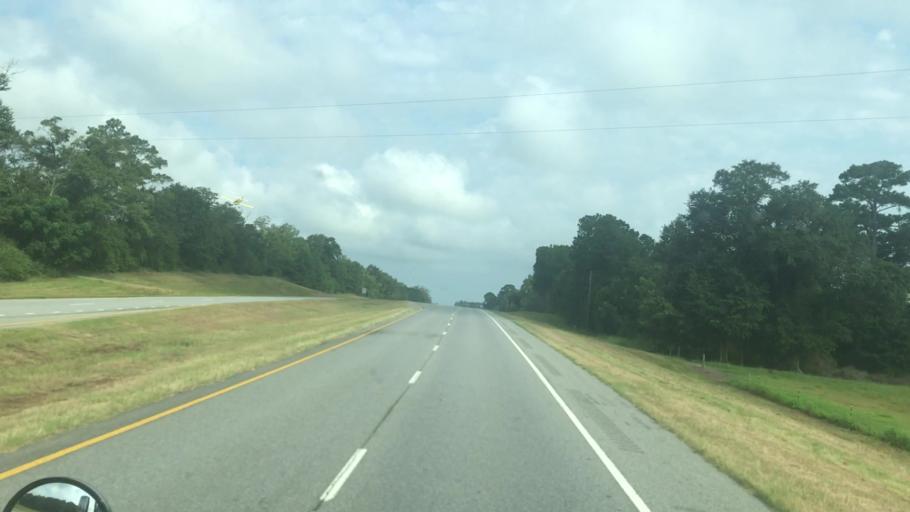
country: US
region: Georgia
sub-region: Miller County
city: Colquitt
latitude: 31.2480
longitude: -84.7949
